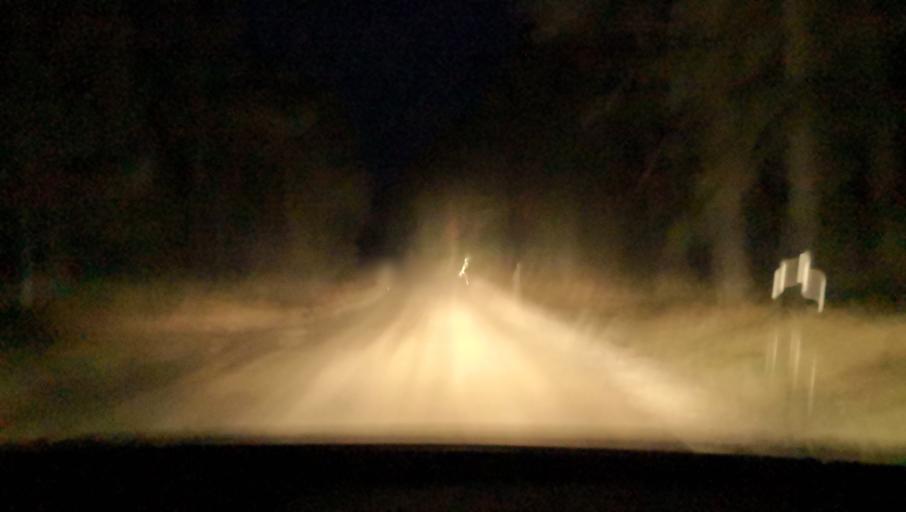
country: SE
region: Vaestmanland
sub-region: Skinnskattebergs Kommun
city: Skinnskatteberg
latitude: 59.6741
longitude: 15.5861
